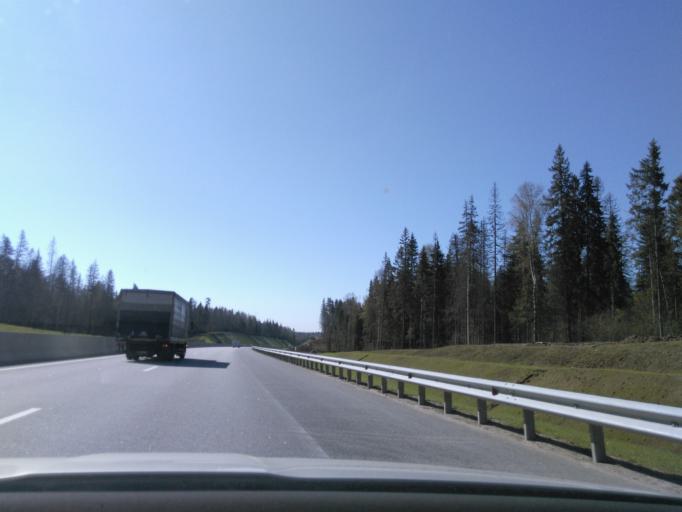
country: RU
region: Moskovskaya
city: Mendeleyevo
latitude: 56.0474
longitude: 37.2631
